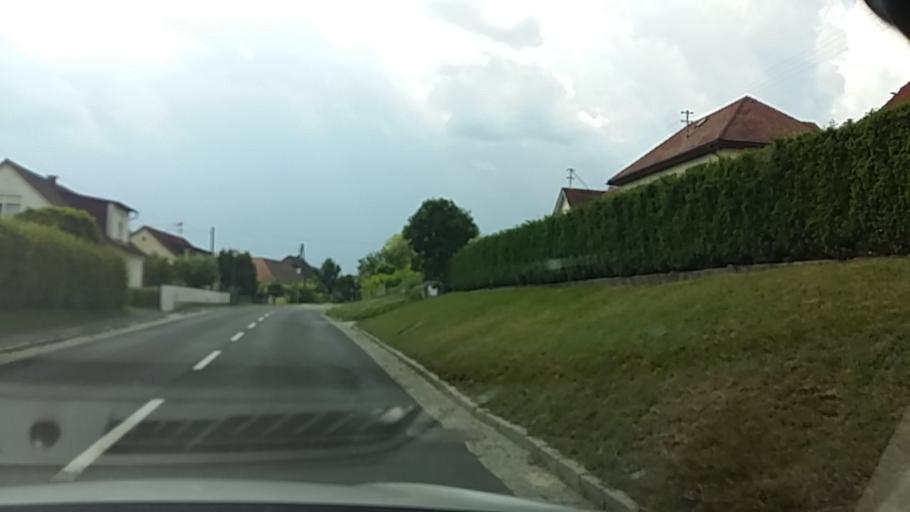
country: AT
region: Styria
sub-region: Politischer Bezirk Hartberg-Fuerstenfeld
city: Soechau
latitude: 47.0326
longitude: 16.0130
